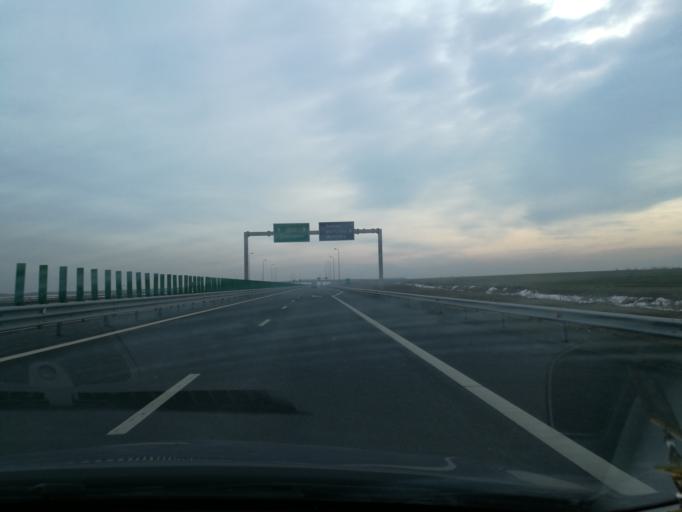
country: RO
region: Constanta
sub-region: Municipiul Medgidia
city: Valea Dacilor
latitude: 44.1800
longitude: 28.3147
